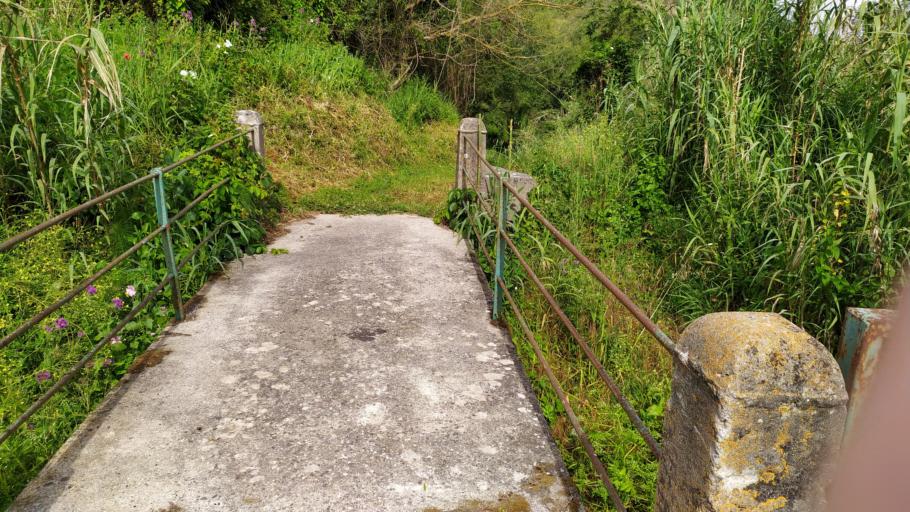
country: IT
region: Sicily
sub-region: Messina
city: San Pier Niceto
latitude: 38.1572
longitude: 15.3497
